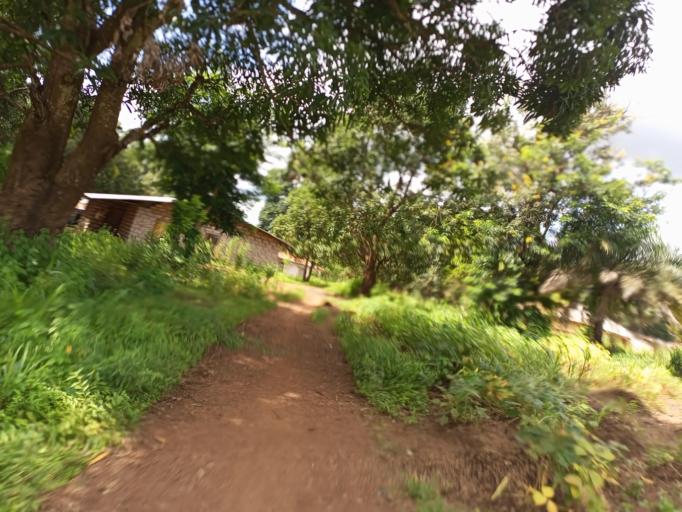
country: SL
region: Northern Province
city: Kamakwie
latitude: 9.4991
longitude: -12.2365
